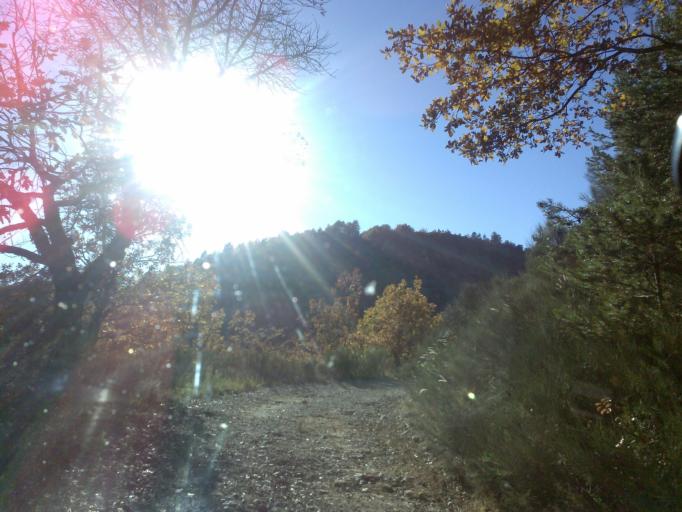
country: FR
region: Provence-Alpes-Cote d'Azur
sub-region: Departement des Alpes-de-Haute-Provence
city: Le Brusquet
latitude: 44.1891
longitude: 6.2616
